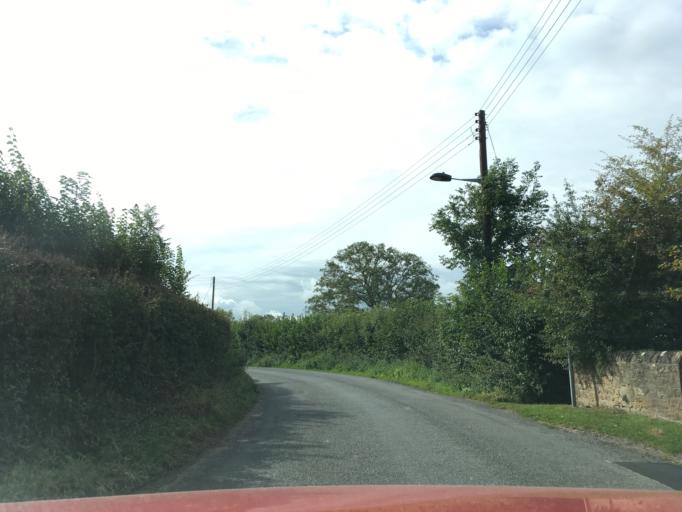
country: GB
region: England
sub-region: South Gloucestershire
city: Thornbury
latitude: 51.6090
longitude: -2.5331
